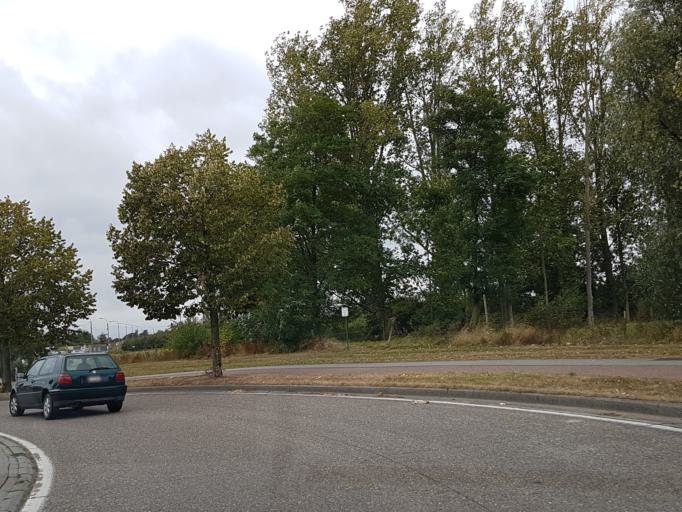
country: BE
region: Flanders
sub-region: Provincie Limburg
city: Sint-Truiden
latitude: 50.8140
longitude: 5.1623
